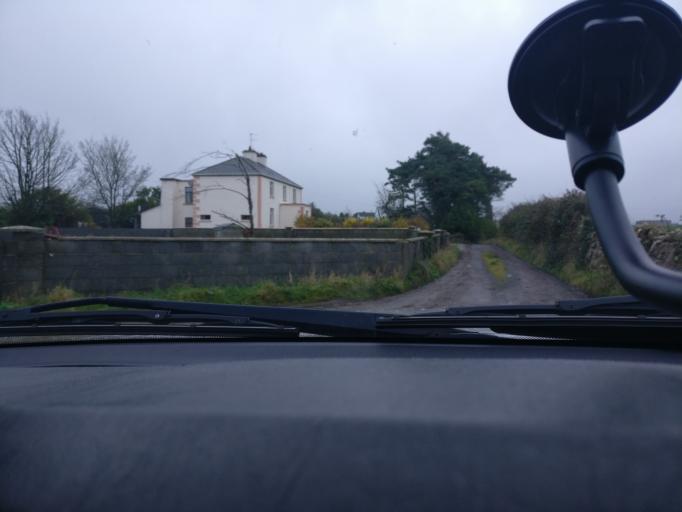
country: IE
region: Connaught
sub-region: County Galway
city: Loughrea
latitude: 53.2077
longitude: -8.5470
